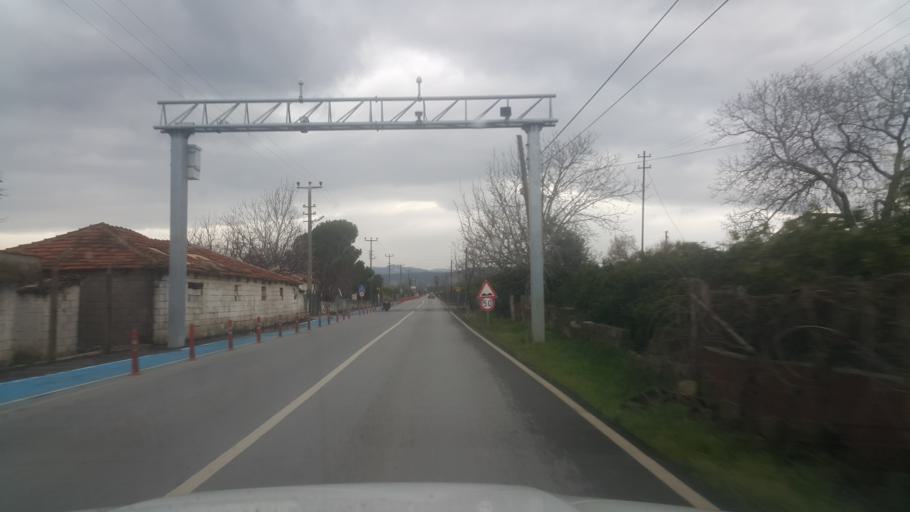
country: TR
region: Izmir
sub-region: Seferihisar
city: Seferhisar
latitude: 38.1890
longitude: 26.8114
